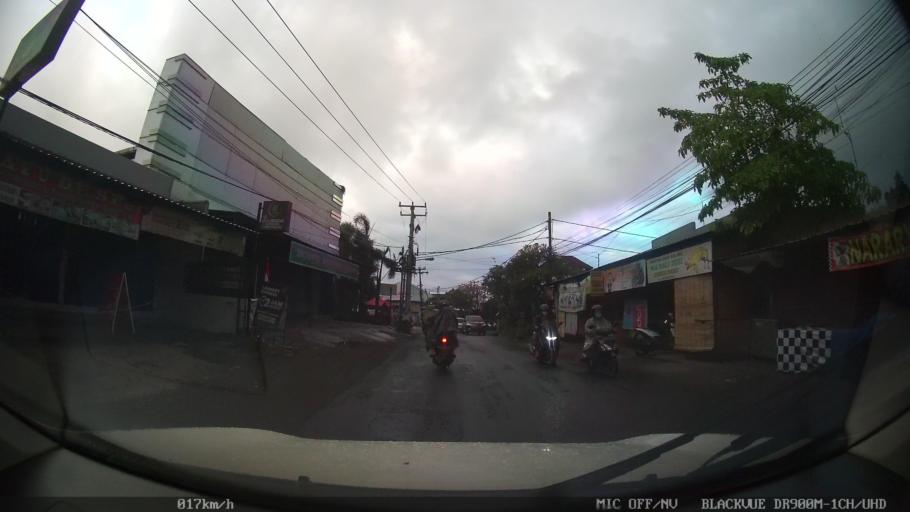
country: ID
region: Bali
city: Banjar Kayangan
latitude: -8.6203
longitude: 115.2229
